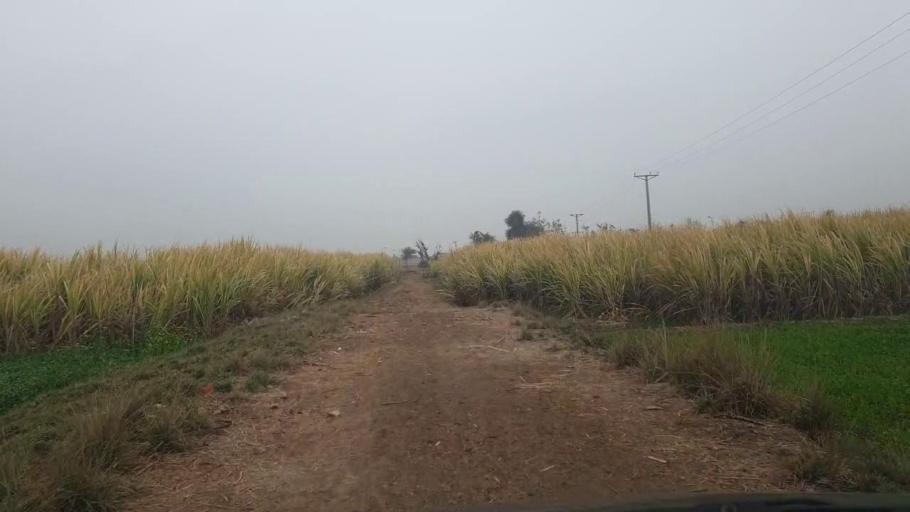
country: PK
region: Sindh
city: Tando Adam
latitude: 25.8022
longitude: 68.6885
